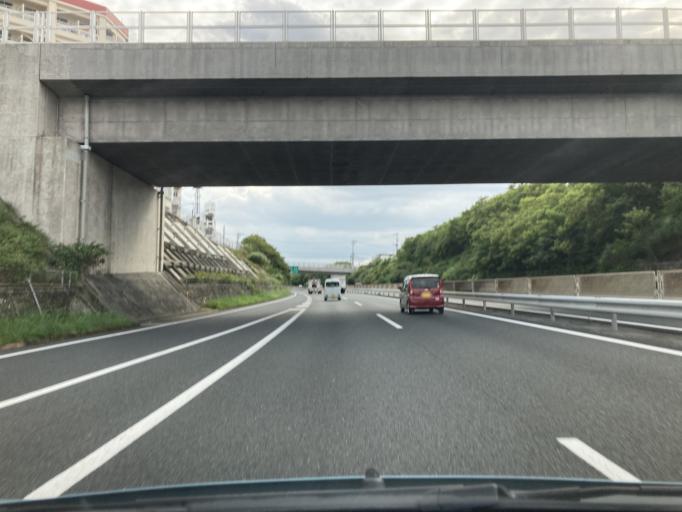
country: JP
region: Okinawa
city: Ginowan
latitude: 26.2552
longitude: 127.7633
